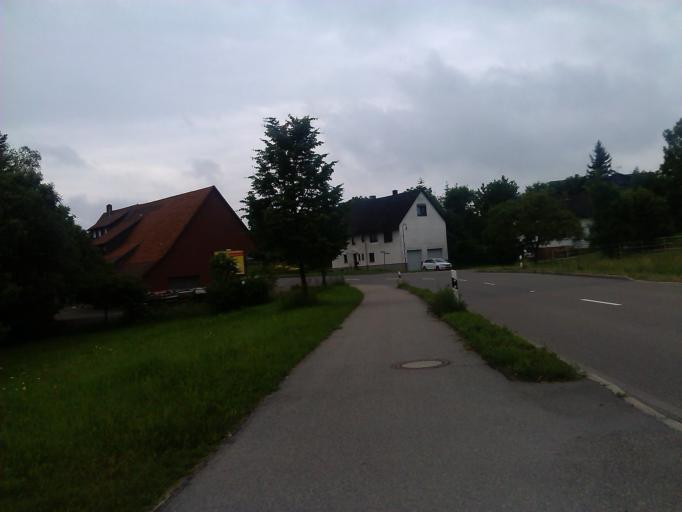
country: DE
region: Baden-Wuerttemberg
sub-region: Regierungsbezirk Stuttgart
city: Mainhardt
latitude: 49.0820
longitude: 9.5310
